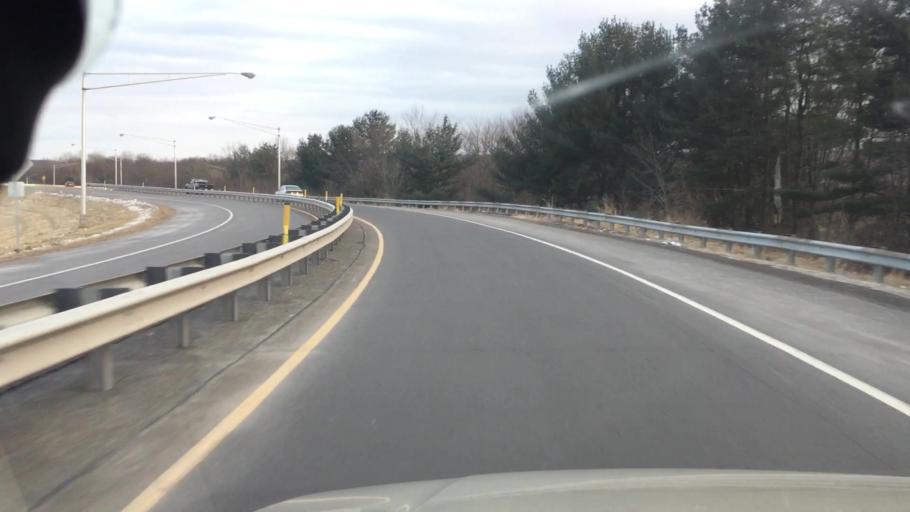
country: US
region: Pennsylvania
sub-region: Luzerne County
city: Nanticoke
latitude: 41.2073
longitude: -75.9827
